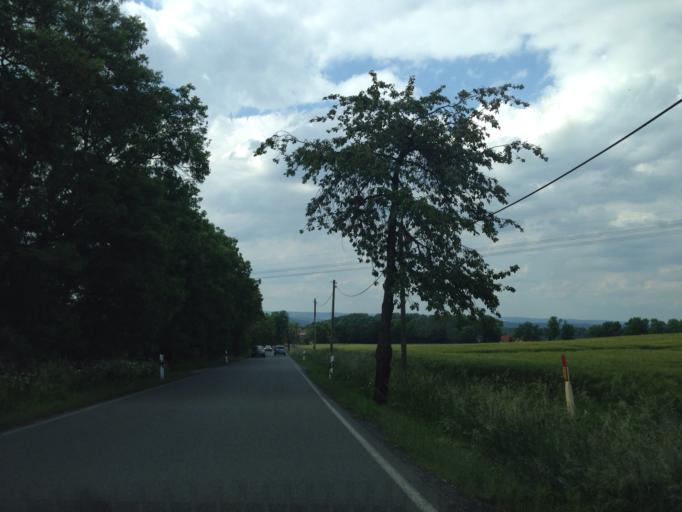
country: DE
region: Thuringia
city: Ranis
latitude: 50.6555
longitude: 11.5759
